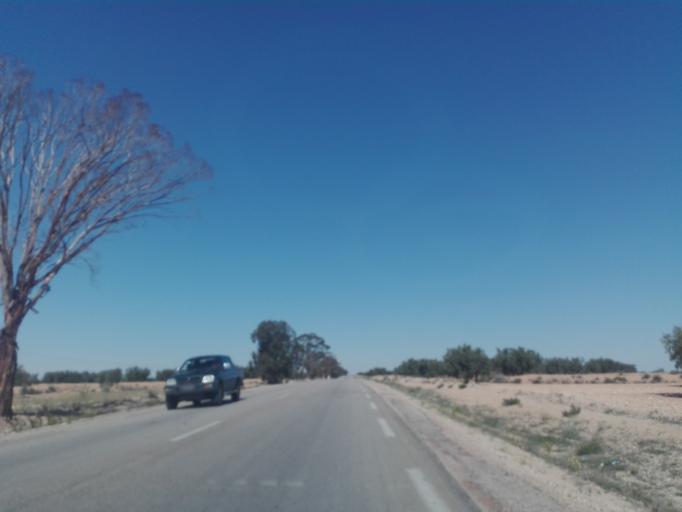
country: TN
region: Safaqis
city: Bi'r `Ali Bin Khalifah
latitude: 34.7515
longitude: 10.3441
